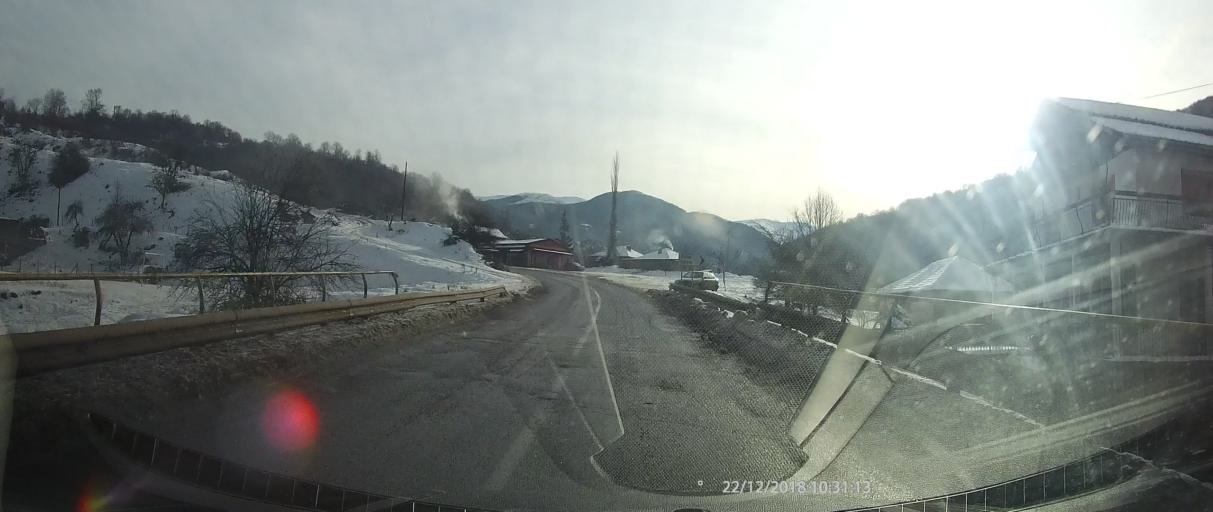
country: MK
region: Kriva Palanka
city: Kriva Palanka
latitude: 42.2230
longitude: 22.4226
